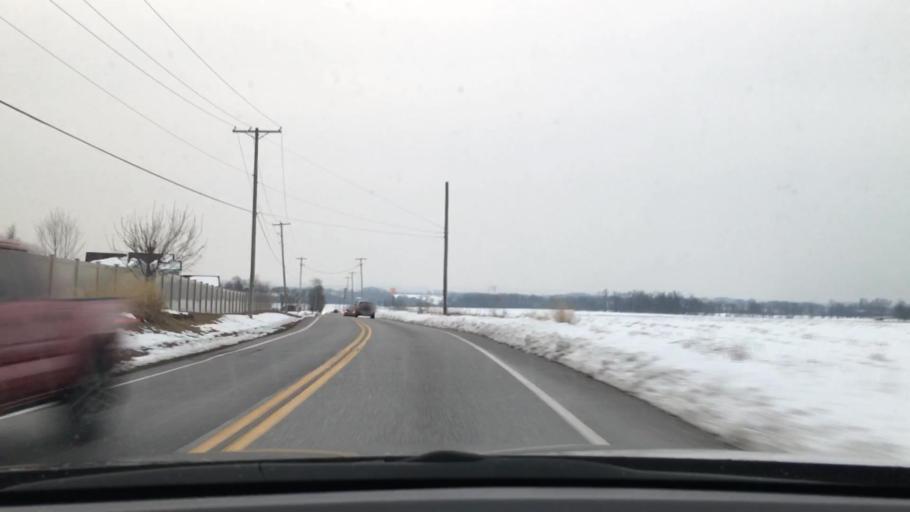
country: US
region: Pennsylvania
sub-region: York County
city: Weigelstown
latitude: 39.9726
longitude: -76.8491
